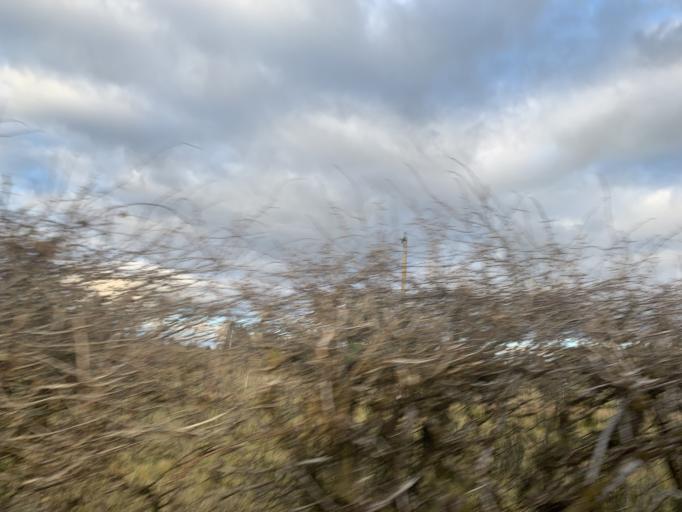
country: IE
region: Connaught
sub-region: Maigh Eo
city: Ballyhaunis
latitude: 53.8313
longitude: -8.7055
